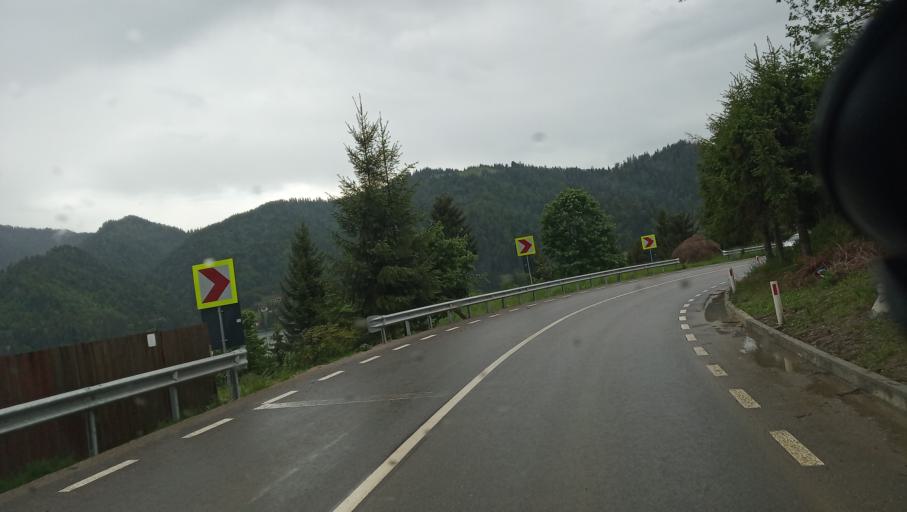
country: RO
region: Bistrita-Nasaud
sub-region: Comuna Tiha Bargaului
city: Tureac
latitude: 47.1723
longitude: 24.8893
